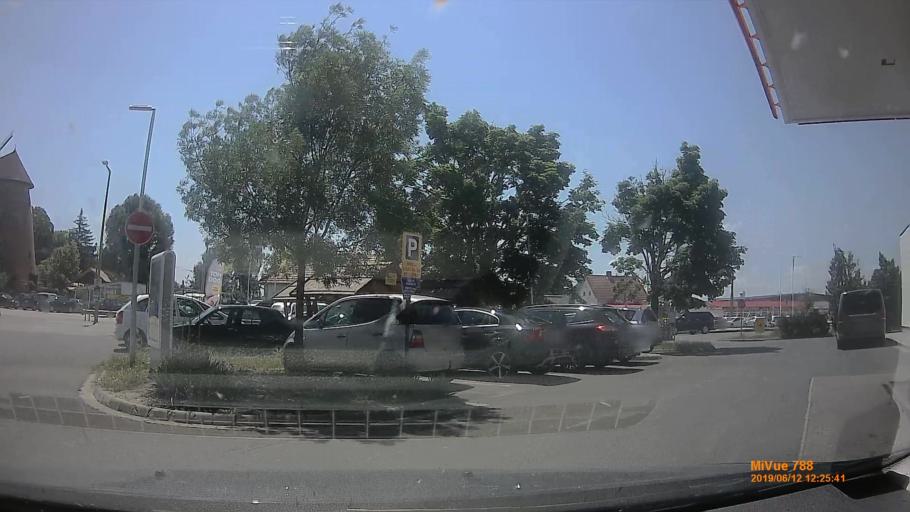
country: HU
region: Bacs-Kiskun
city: Kecskemet
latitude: 46.8817
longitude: 19.7072
